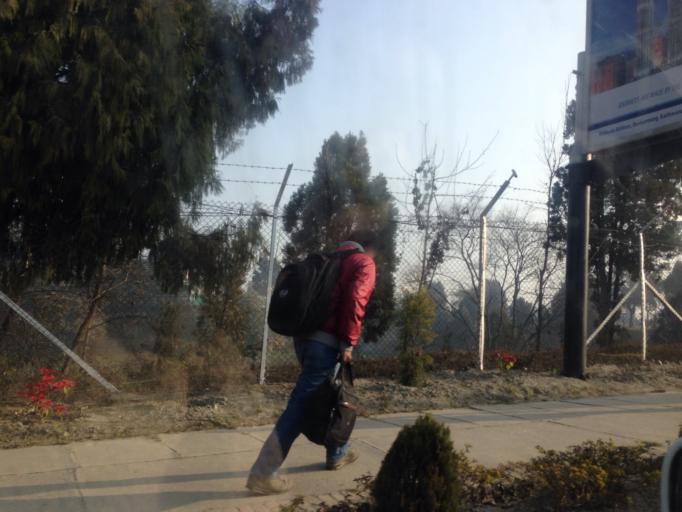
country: NP
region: Central Region
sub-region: Bagmati Zone
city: Kathmandu
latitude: 27.7010
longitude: 85.3555
